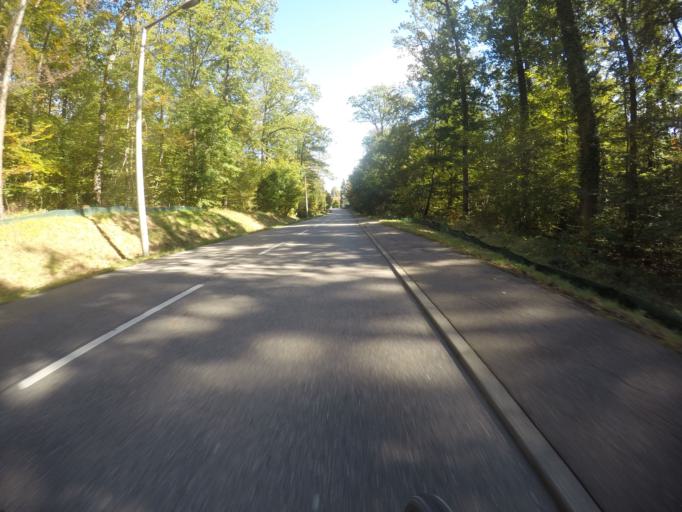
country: DE
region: Baden-Wuerttemberg
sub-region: Regierungsbezirk Stuttgart
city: Stuttgart-Ost
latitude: 48.7616
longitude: 9.2125
